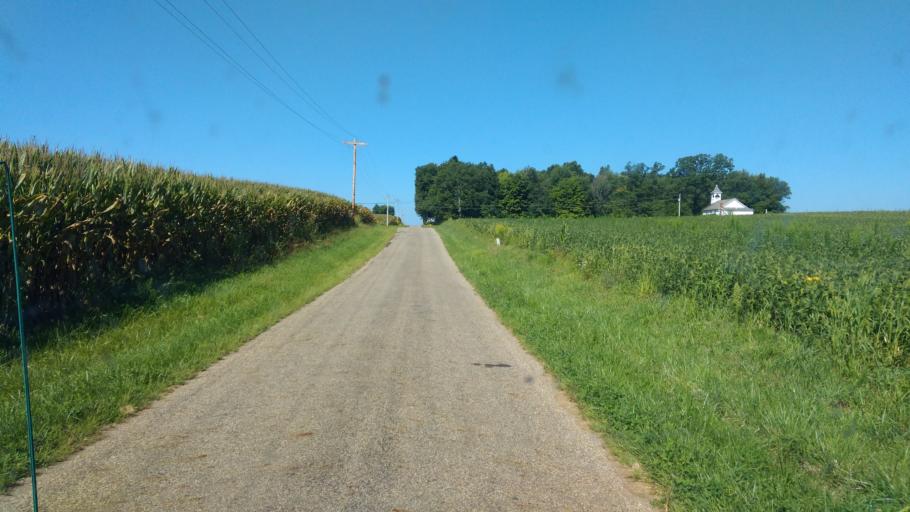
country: US
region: Ohio
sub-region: Knox County
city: Mount Vernon
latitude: 40.4558
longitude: -82.4695
